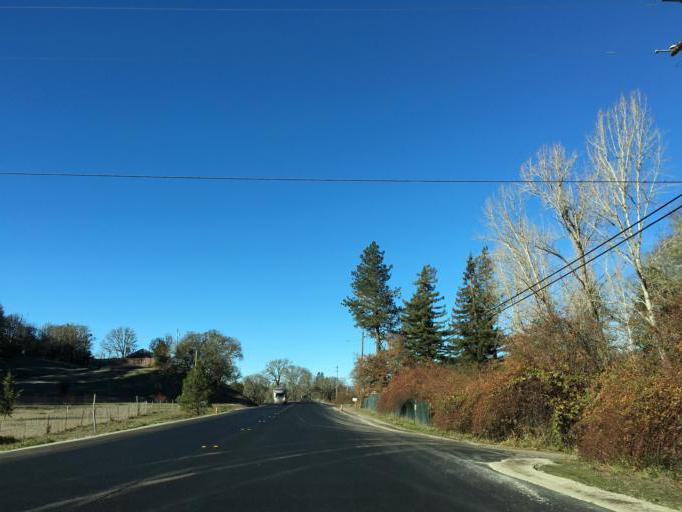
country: US
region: California
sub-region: Mendocino County
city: Laytonville
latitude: 39.6383
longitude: -123.4702
